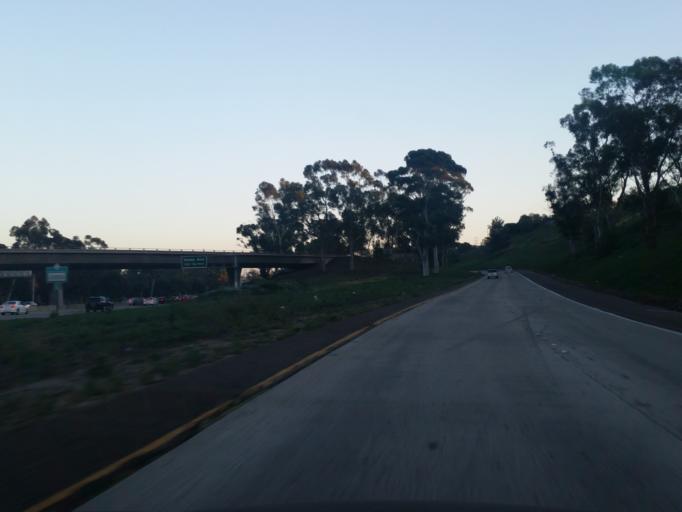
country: US
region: California
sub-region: San Diego County
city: San Diego
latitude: 32.7389
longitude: -117.1156
